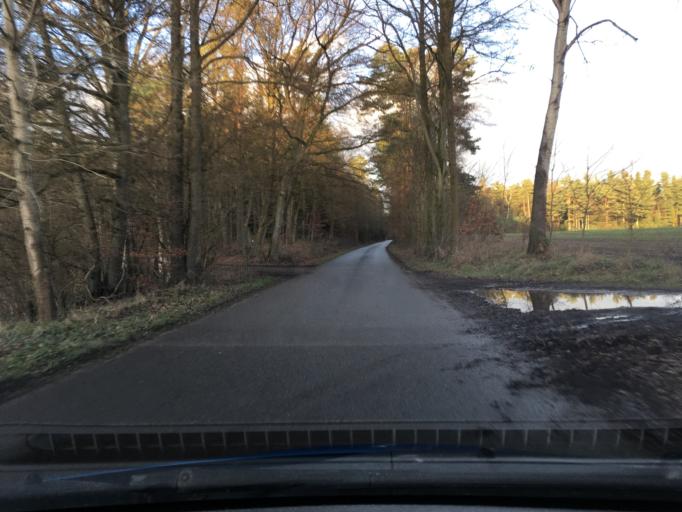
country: DE
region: Lower Saxony
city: Soderstorf
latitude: 53.0943
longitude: 10.1520
